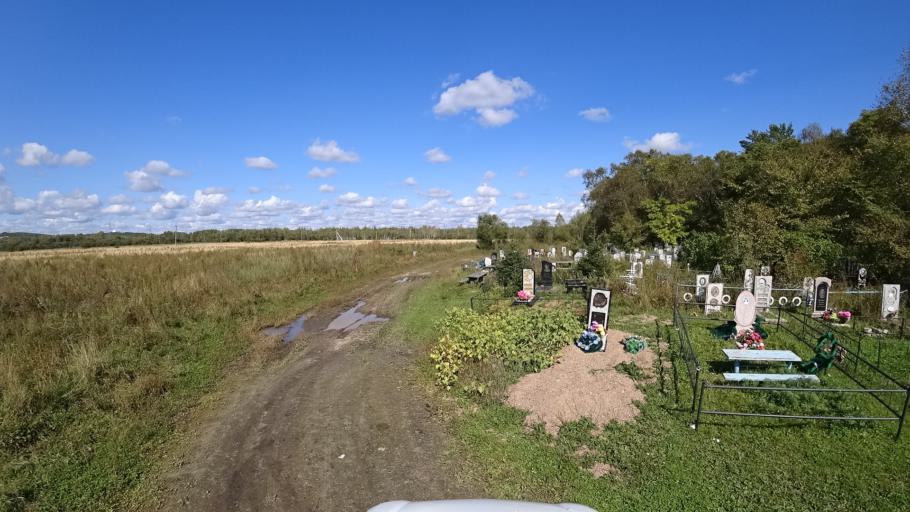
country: RU
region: Amur
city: Arkhara
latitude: 49.4002
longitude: 130.1209
